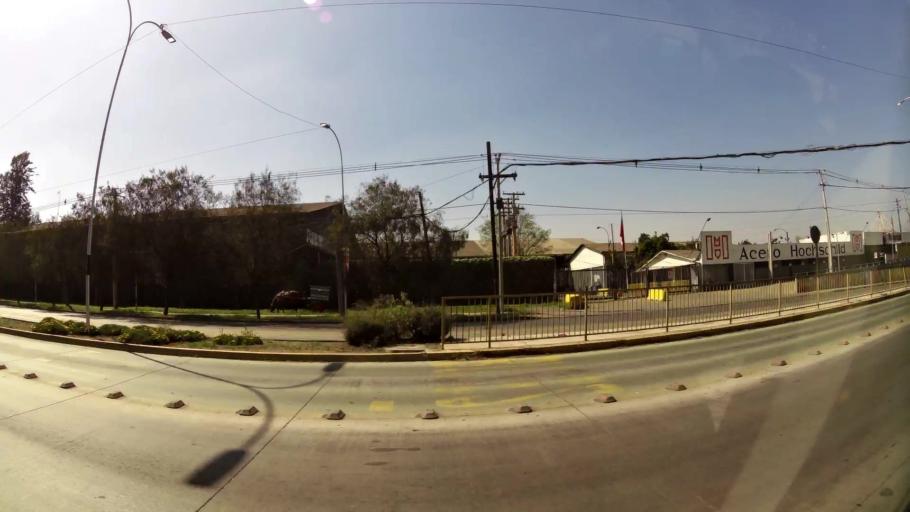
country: CL
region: Santiago Metropolitan
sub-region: Provincia de Santiago
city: Lo Prado
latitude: -33.4012
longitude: -70.6917
